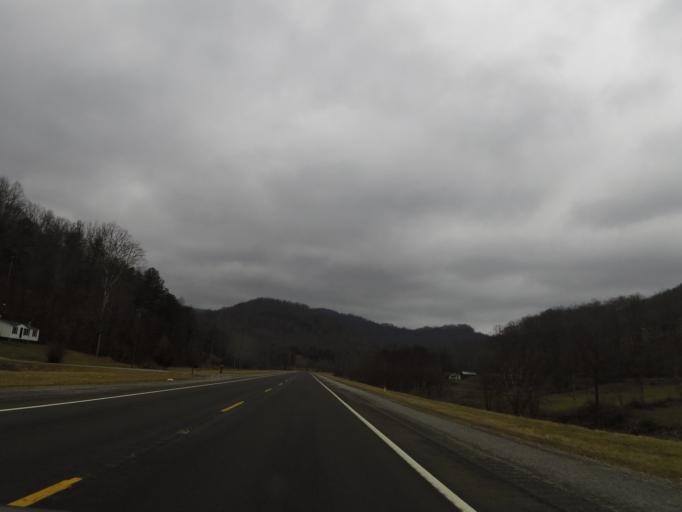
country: US
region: Tennessee
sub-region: Campbell County
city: Caryville
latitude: 36.3861
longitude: -84.3430
